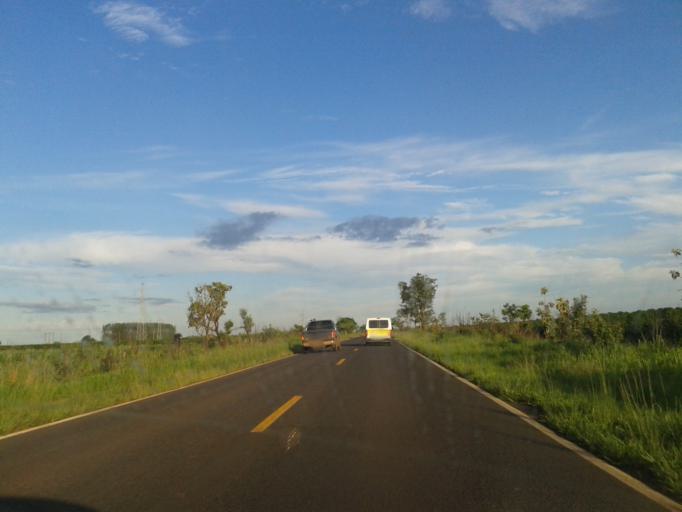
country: BR
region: Minas Gerais
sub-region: Araguari
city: Araguari
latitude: -18.6277
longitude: -48.2353
